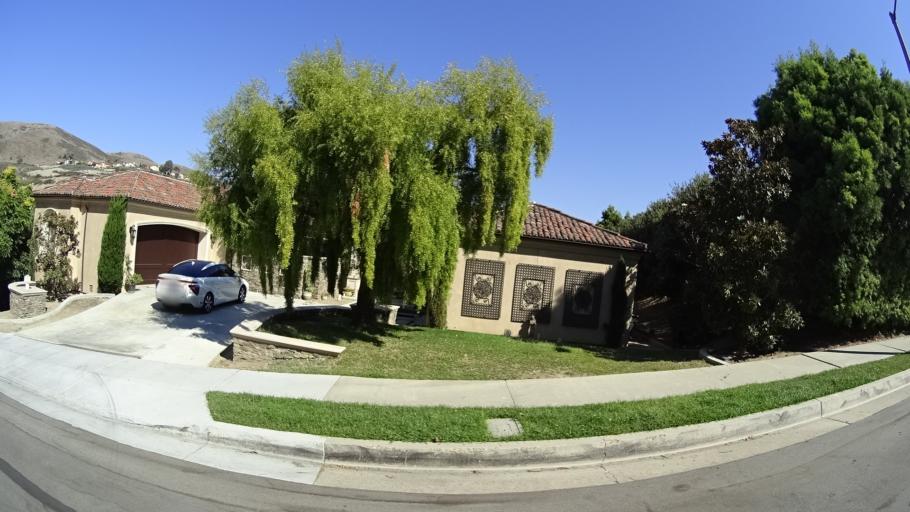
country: US
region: California
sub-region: Orange County
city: San Juan Capistrano
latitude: 33.4651
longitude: -117.6374
